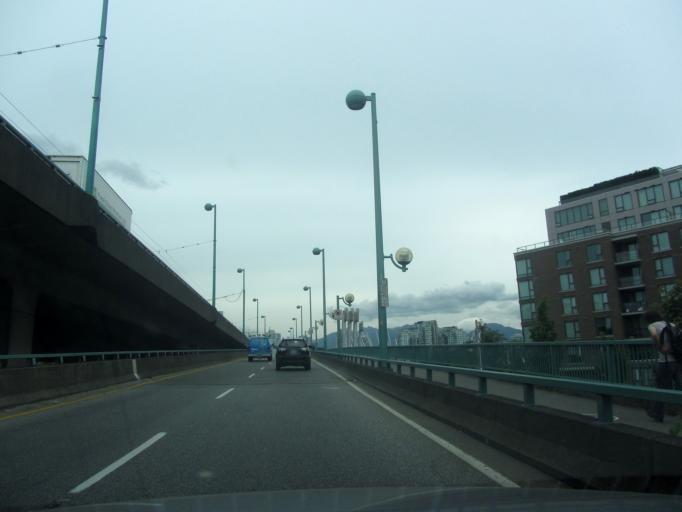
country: CA
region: British Columbia
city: Vancouver
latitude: 49.2692
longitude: -123.1015
